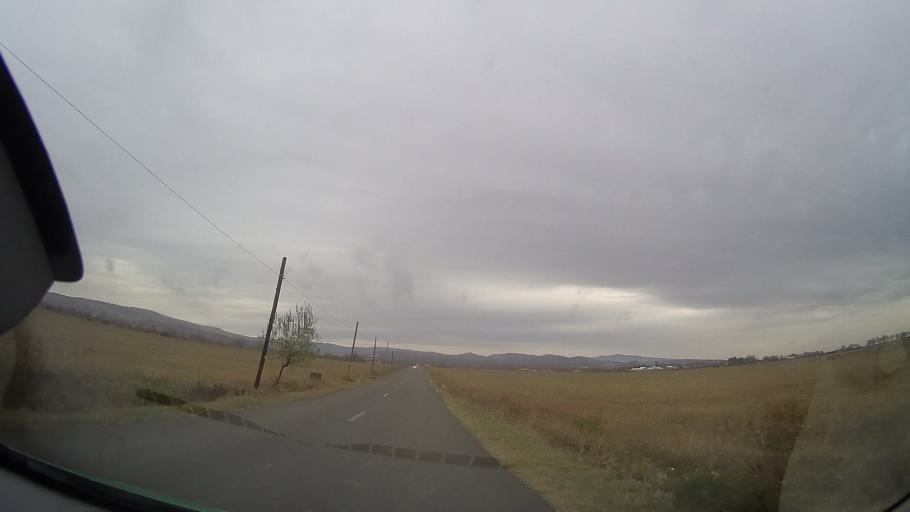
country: RO
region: Prahova
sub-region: Comuna Fantanele
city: Fantanele
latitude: 45.0225
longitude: 26.3809
